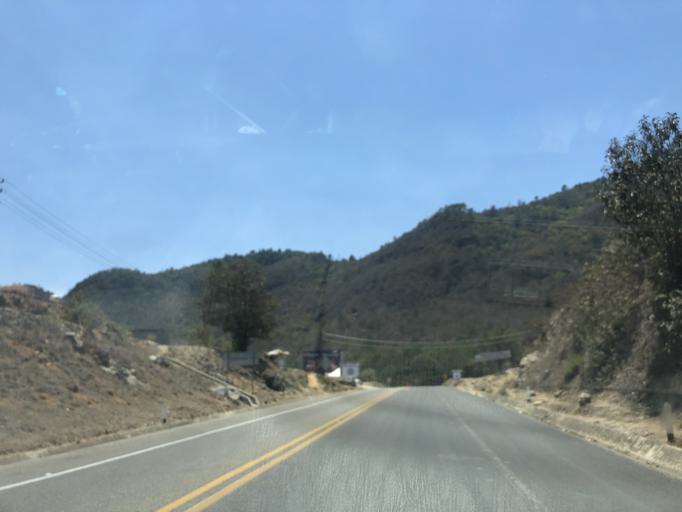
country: MX
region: Chiapas
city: San Cristobal de las Casas
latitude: 16.7201
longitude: -92.6550
